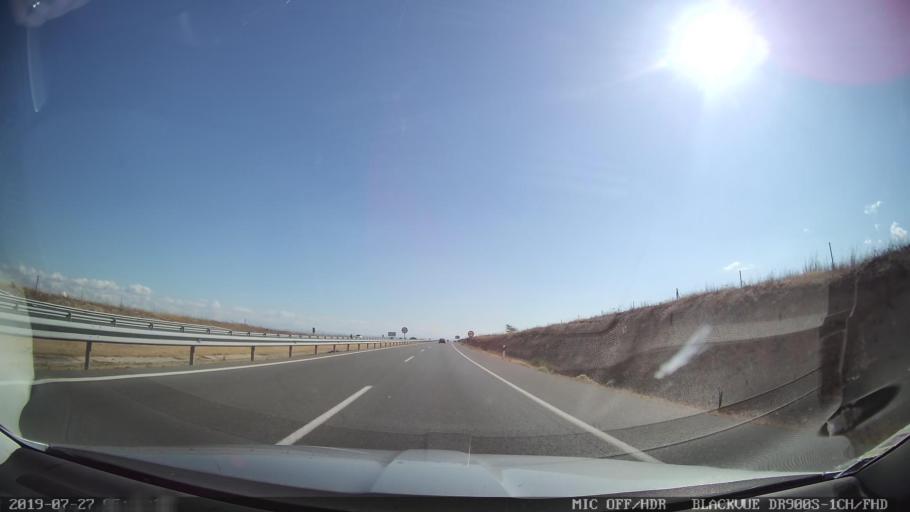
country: ES
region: Castille-La Mancha
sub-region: Province of Toledo
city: Quismondo
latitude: 40.0977
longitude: -4.3375
